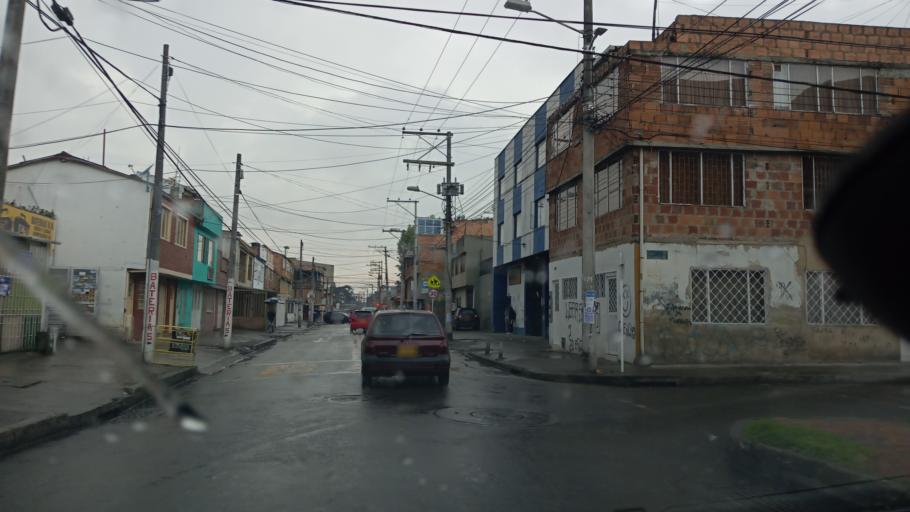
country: CO
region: Cundinamarca
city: Funza
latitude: 4.6789
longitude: -74.1465
